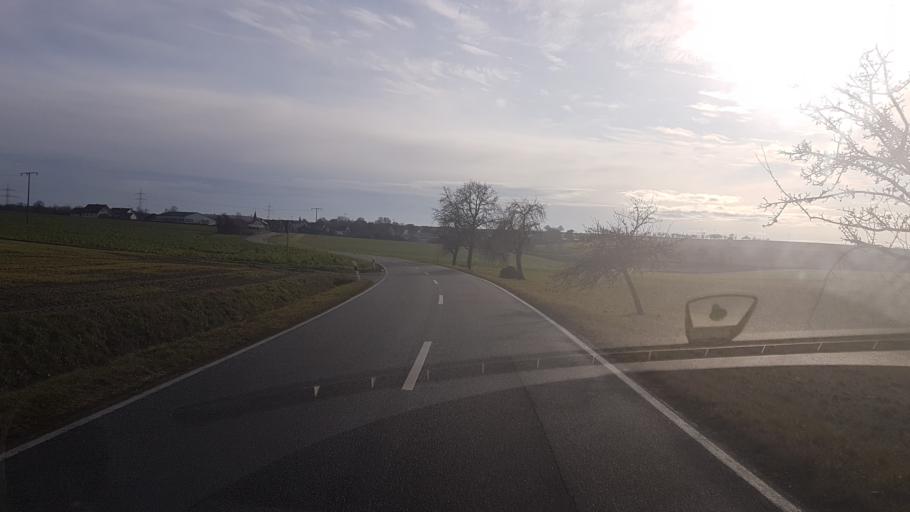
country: DE
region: Baden-Wuerttemberg
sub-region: Regierungsbezirk Stuttgart
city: Kupferzell
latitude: 49.2081
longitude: 9.7342
